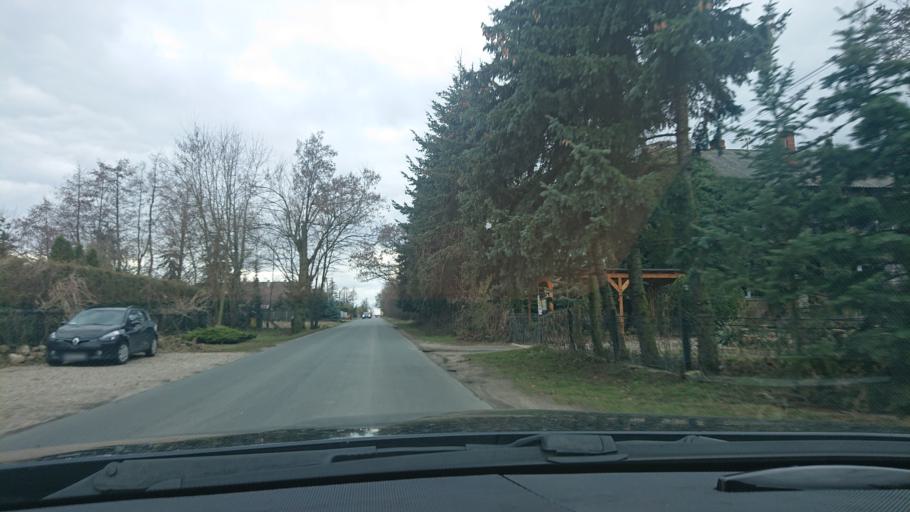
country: PL
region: Greater Poland Voivodeship
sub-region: Powiat gnieznienski
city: Gniezno
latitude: 52.5752
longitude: 17.6240
